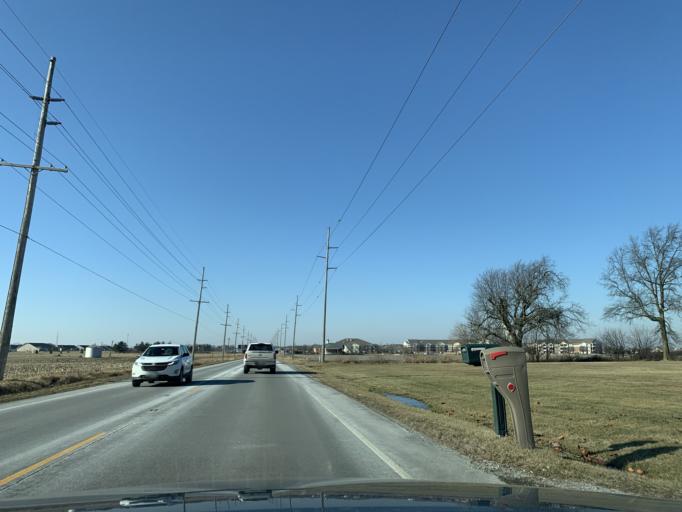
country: US
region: Indiana
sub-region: Lake County
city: Saint John
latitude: 41.4210
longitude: -87.4359
